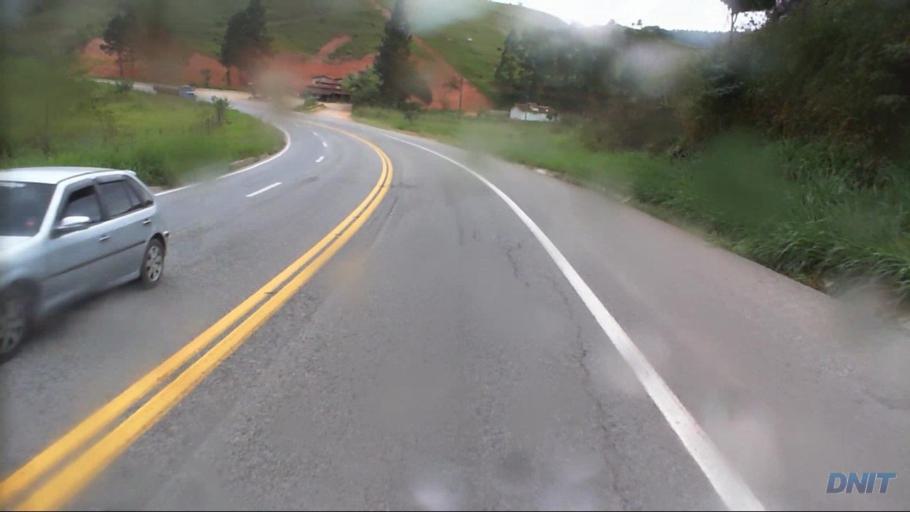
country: BR
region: Minas Gerais
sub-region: Nova Era
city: Nova Era
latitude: -19.6949
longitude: -42.9954
